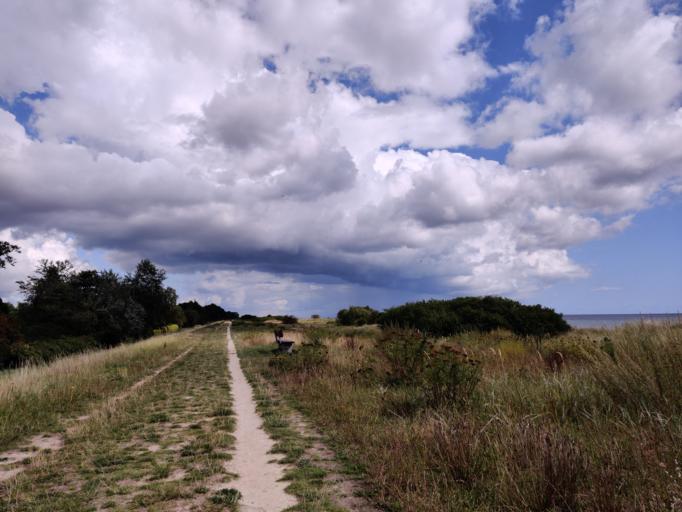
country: DK
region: Zealand
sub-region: Guldborgsund Kommune
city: Nykobing Falster
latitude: 54.7086
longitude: 11.9869
